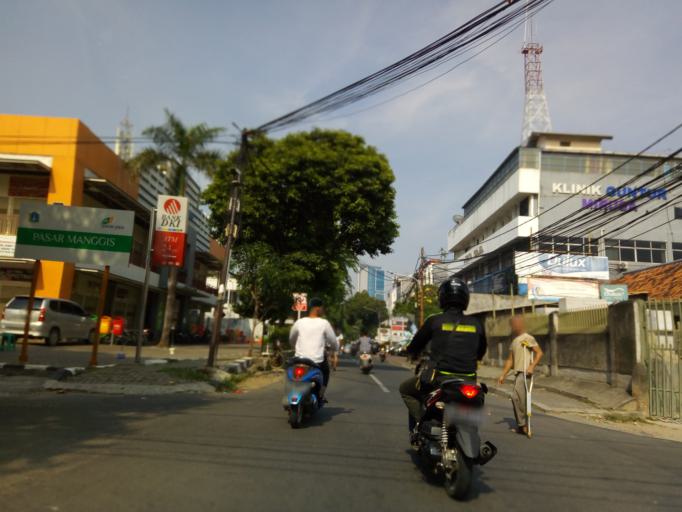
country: ID
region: Jakarta Raya
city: Jakarta
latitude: -6.2077
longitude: 106.8377
